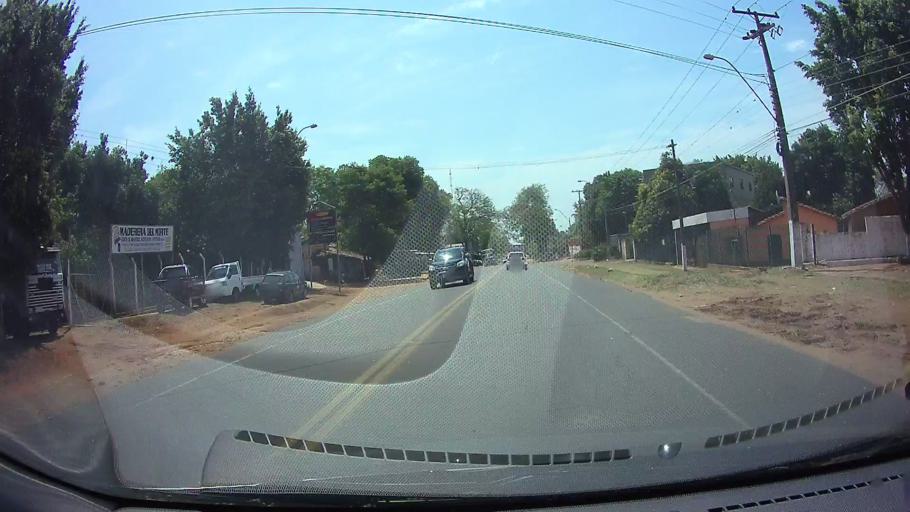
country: PY
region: Central
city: Capiata
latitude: -25.4078
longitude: -57.4609
